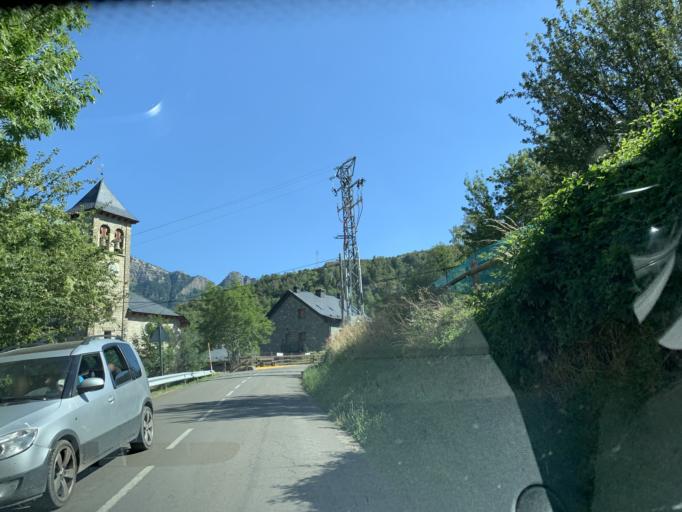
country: ES
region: Aragon
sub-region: Provincia de Huesca
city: Hoz de Jaca
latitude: 42.6967
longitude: -0.3248
